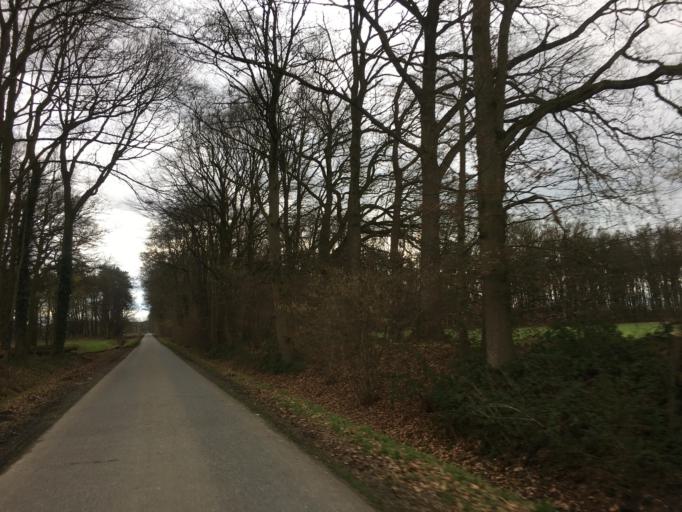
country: DE
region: North Rhine-Westphalia
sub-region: Regierungsbezirk Munster
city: Muenster
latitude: 52.0241
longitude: 7.6360
